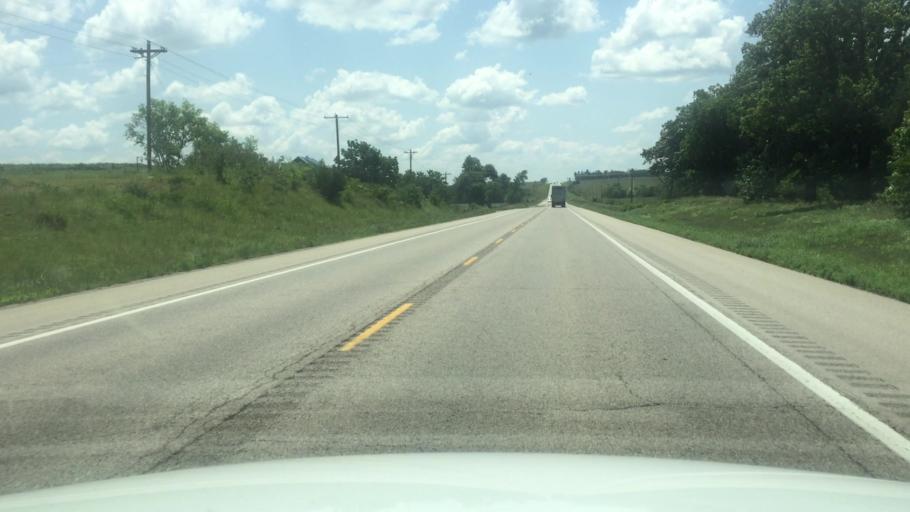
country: US
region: Kansas
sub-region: Brown County
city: Horton
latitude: 39.6886
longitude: -95.7304
